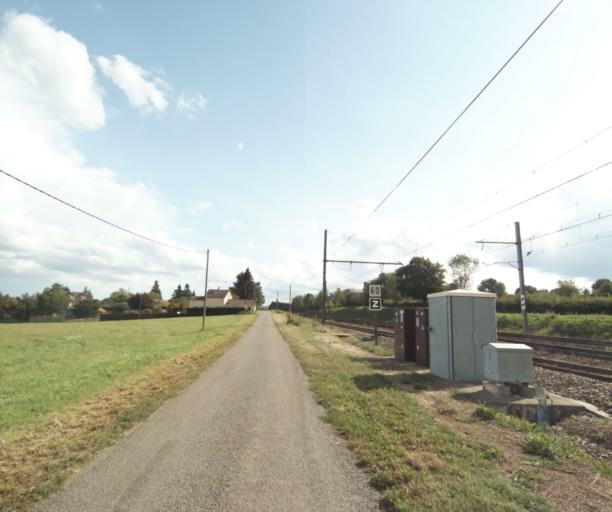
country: FR
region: Bourgogne
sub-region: Departement de Saone-et-Loire
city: Tournus
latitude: 46.5794
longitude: 4.9054
